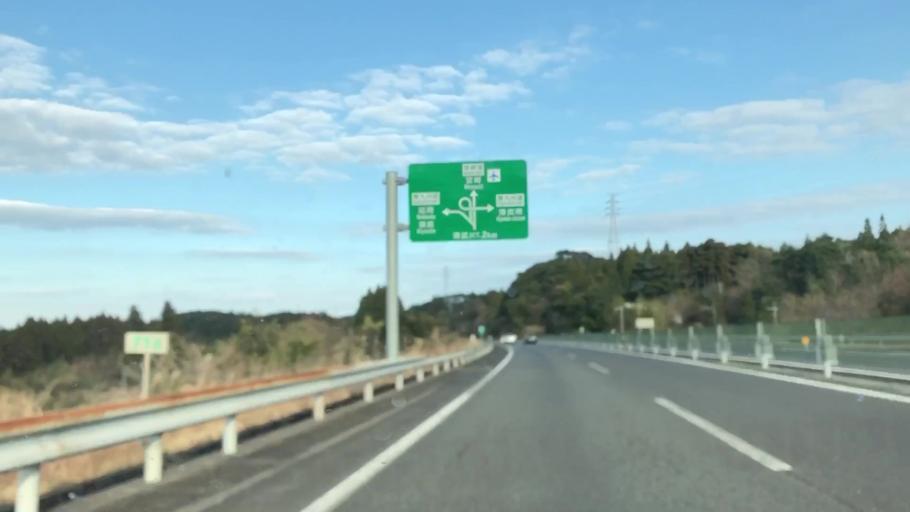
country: JP
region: Miyazaki
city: Miyazaki-shi
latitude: 31.8339
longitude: 131.3396
